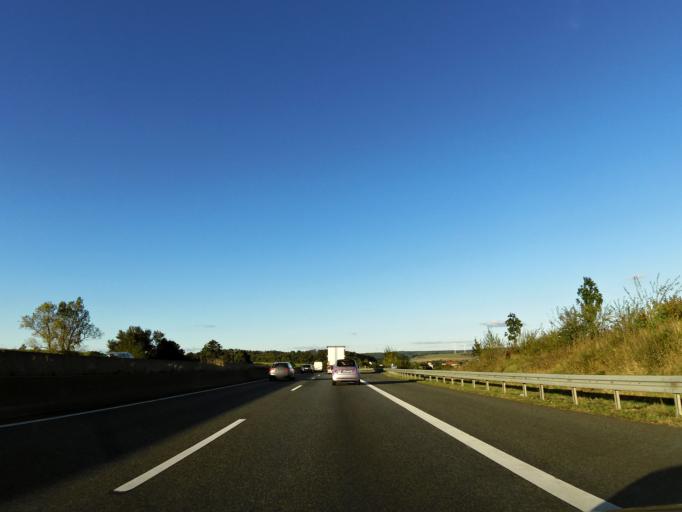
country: DE
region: Hesse
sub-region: Regierungsbezirk Giessen
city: Homberg
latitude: 50.6755
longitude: 9.0276
